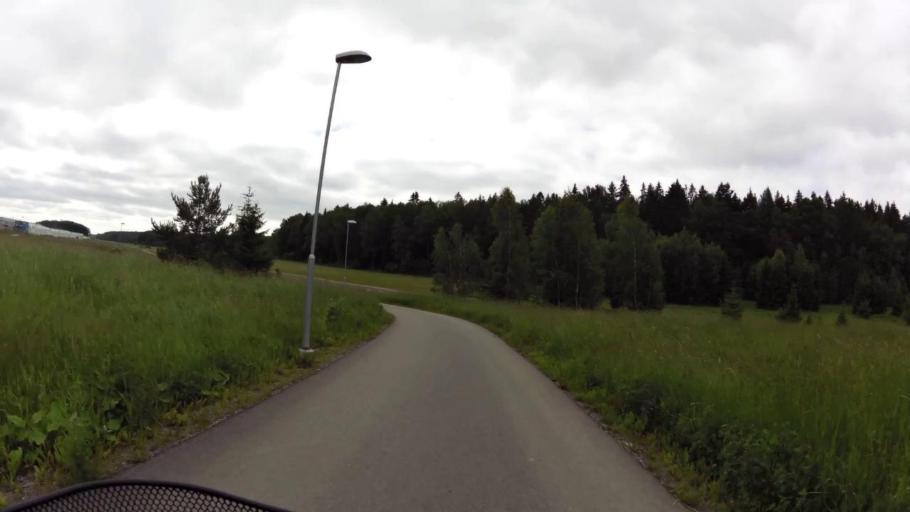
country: SE
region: OEstergoetland
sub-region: Linkopings Kommun
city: Linkoping
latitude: 58.3673
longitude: 15.6715
